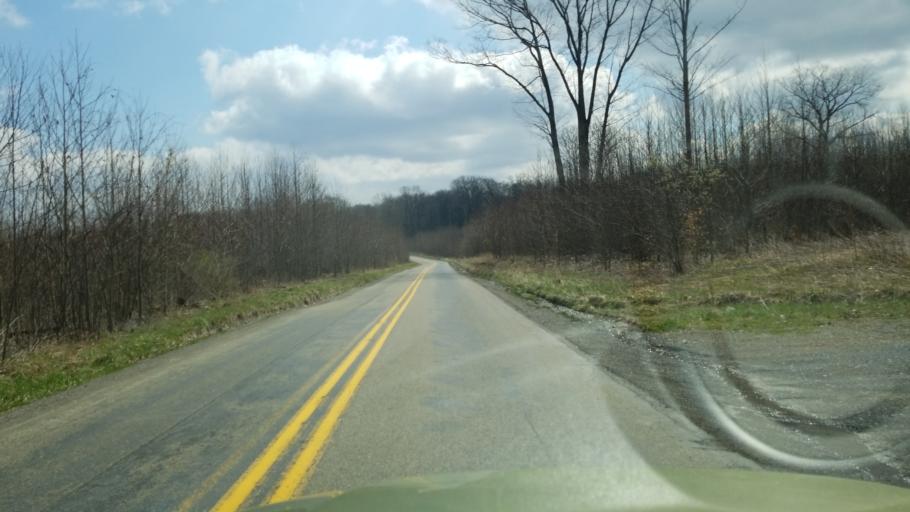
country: US
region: Pennsylvania
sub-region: Jefferson County
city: Brockway
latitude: 41.2786
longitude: -78.8617
